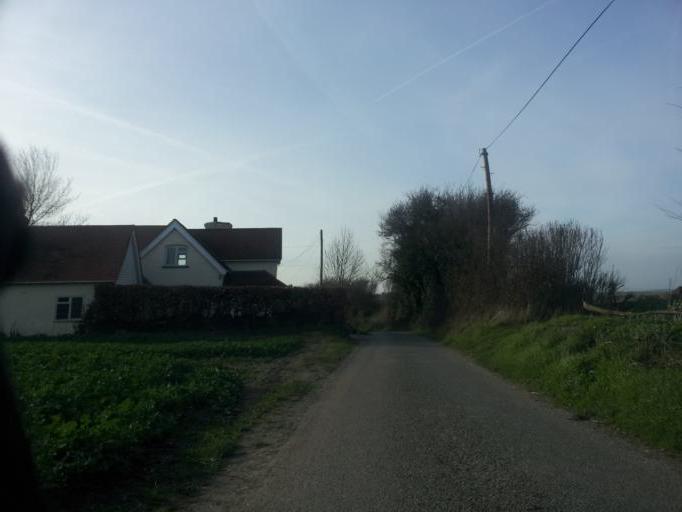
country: GB
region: England
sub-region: Kent
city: Faversham
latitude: 51.3287
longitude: 0.8518
